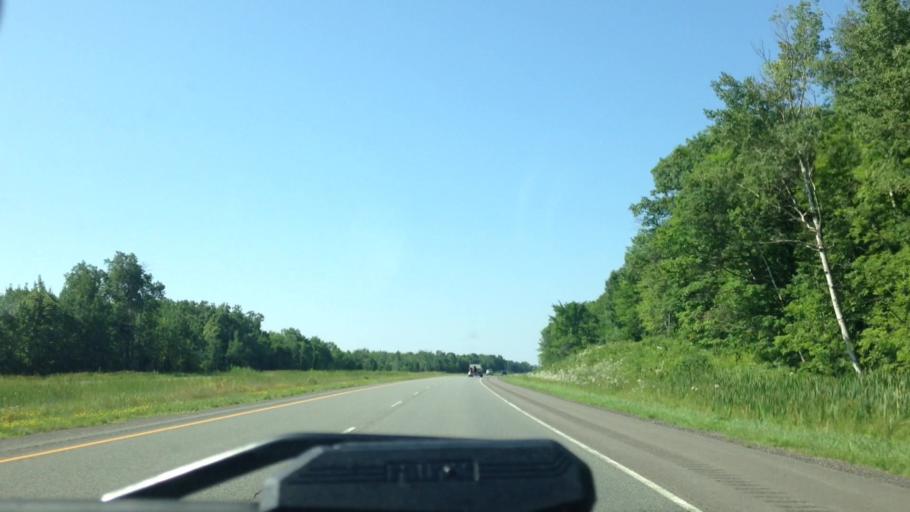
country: US
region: Wisconsin
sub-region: Douglas County
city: Lake Nebagamon
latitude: 46.4128
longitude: -91.8109
